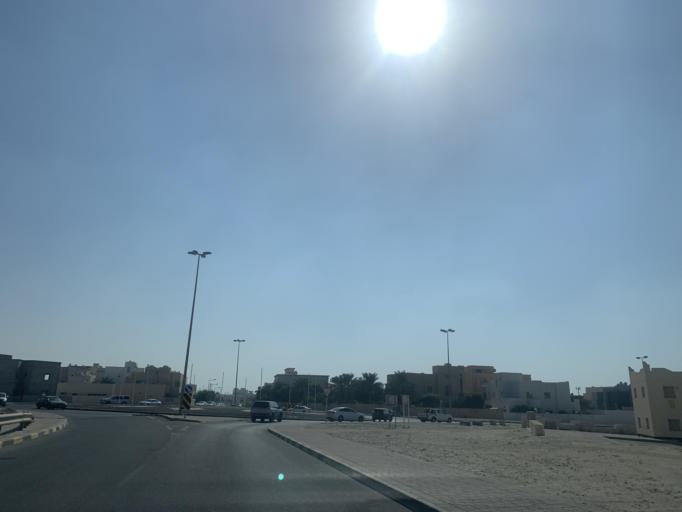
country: BH
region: Central Governorate
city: Madinat Hamad
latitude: 26.1166
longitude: 50.4995
